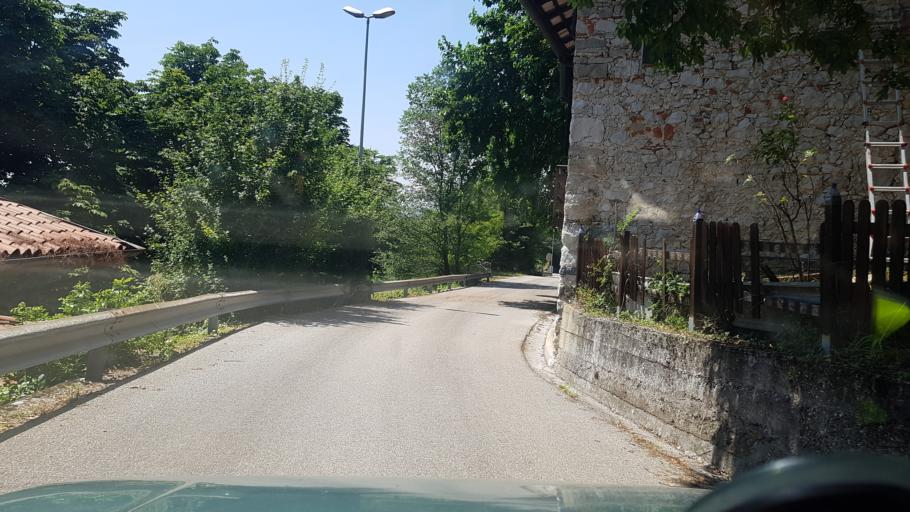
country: IT
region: Friuli Venezia Giulia
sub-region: Provincia di Udine
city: Nimis
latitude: 46.2215
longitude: 13.2630
